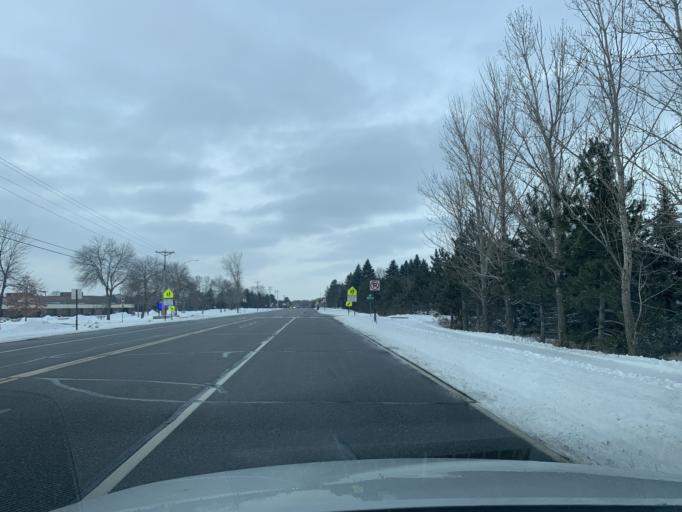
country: US
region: Minnesota
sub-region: Anoka County
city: Ramsey
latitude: 45.2429
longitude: -93.4120
